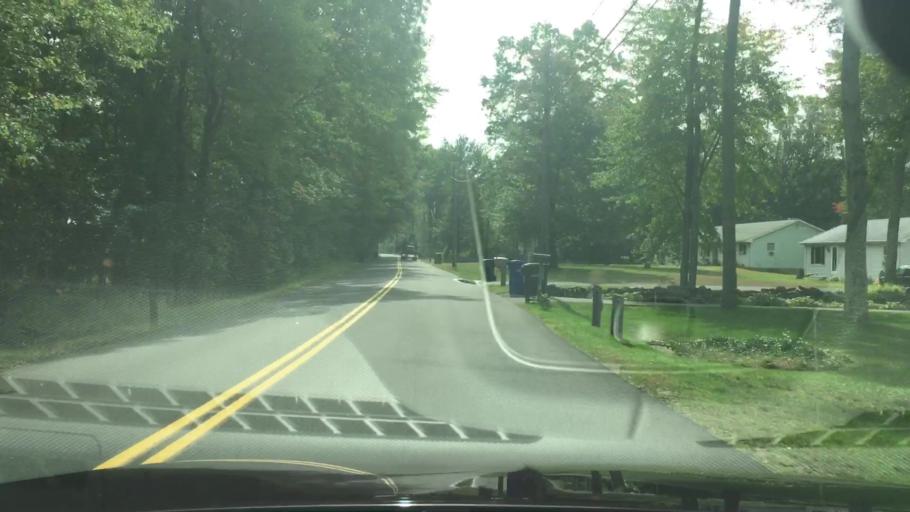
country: US
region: Connecticut
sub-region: Tolland County
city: Ellington
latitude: 41.9444
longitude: -72.4808
